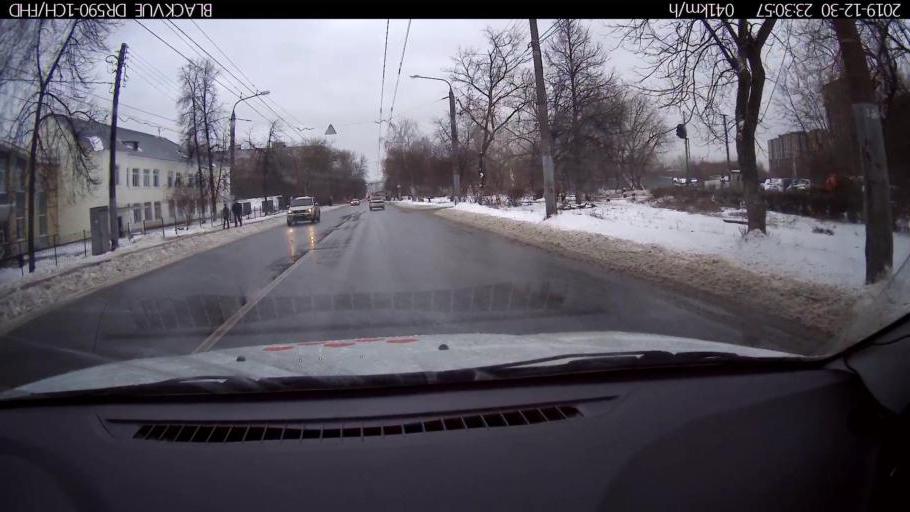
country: RU
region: Nizjnij Novgorod
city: Nizhniy Novgorod
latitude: 56.2762
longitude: 43.9352
